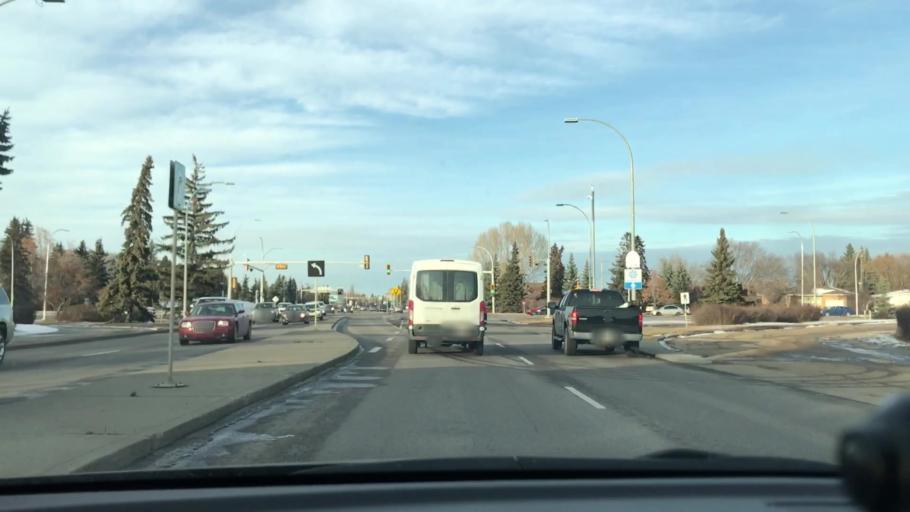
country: CA
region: Alberta
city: Edmonton
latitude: 53.5366
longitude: -113.4429
